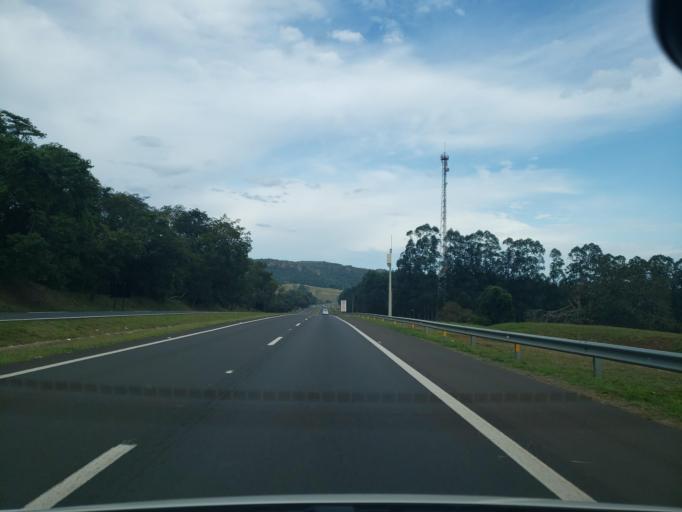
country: BR
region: Sao Paulo
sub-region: Itirapina
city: Itirapina
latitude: -22.2691
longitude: -47.9370
